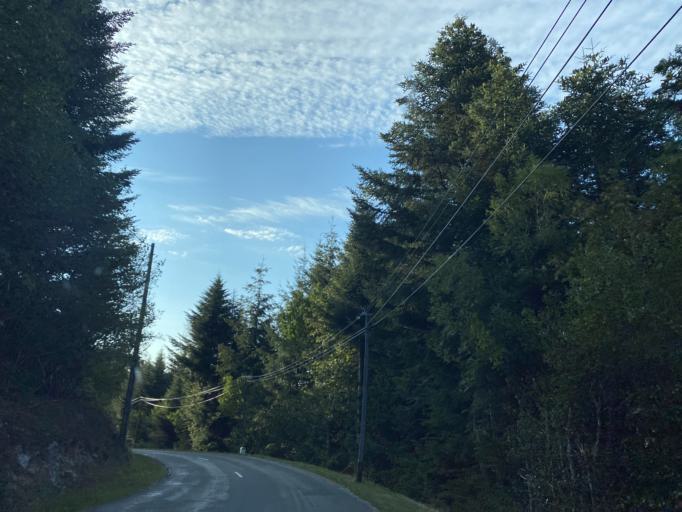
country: FR
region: Rhone-Alpes
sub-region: Departement de la Loire
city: Noiretable
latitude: 45.7938
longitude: 3.7391
